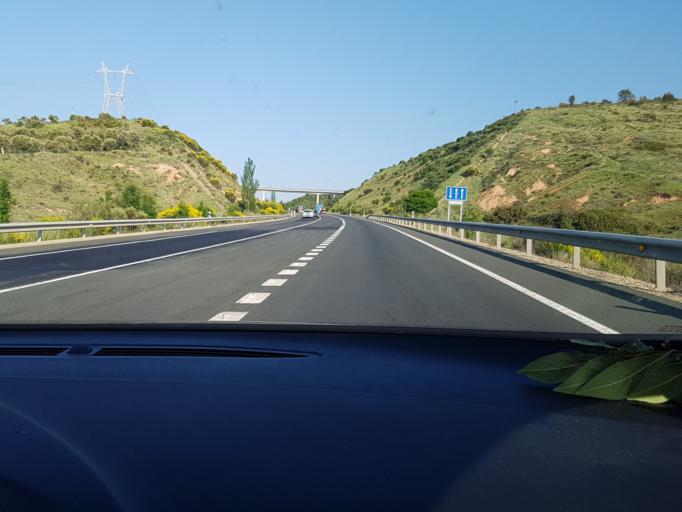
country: ES
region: La Rioja
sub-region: Provincia de La Rioja
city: Ausejo
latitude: 42.3360
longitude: -2.1681
